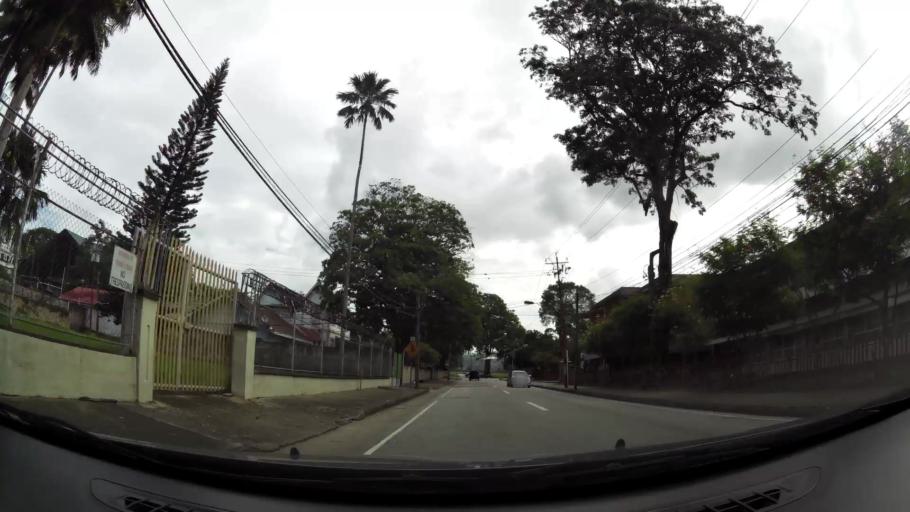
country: TT
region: City of Port of Spain
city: Port-of-Spain
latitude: 10.6695
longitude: -61.5198
